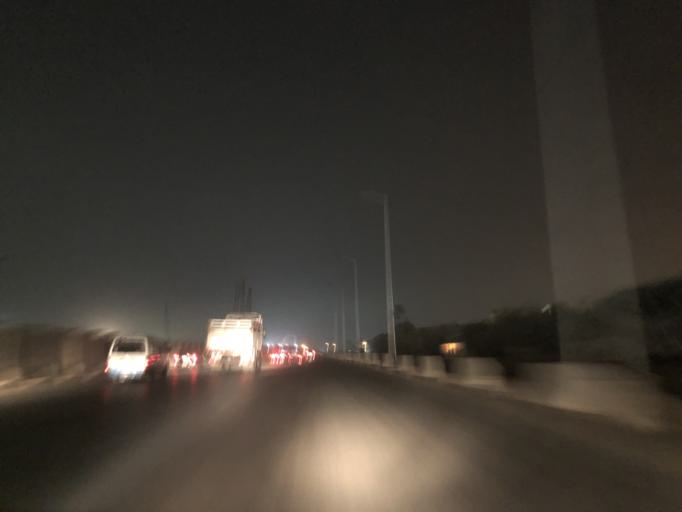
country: EG
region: Al Jizah
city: Madinat Sittah Uktubar
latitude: 29.9572
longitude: 31.0637
